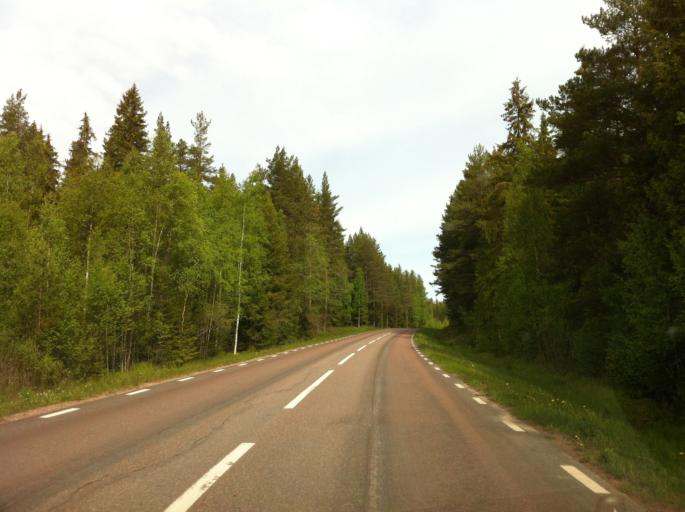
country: SE
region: Dalarna
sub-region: Leksand Municipality
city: Siljansnas
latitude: 60.7636
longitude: 14.7315
